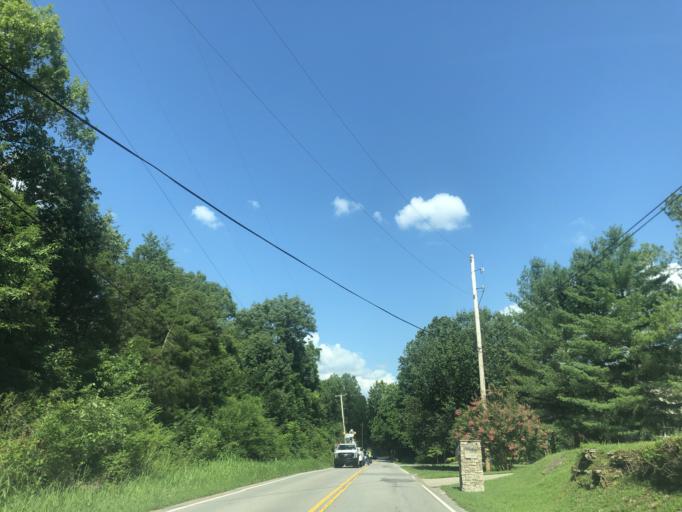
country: US
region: Tennessee
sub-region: Wilson County
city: Green Hill
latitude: 36.1999
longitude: -86.5839
